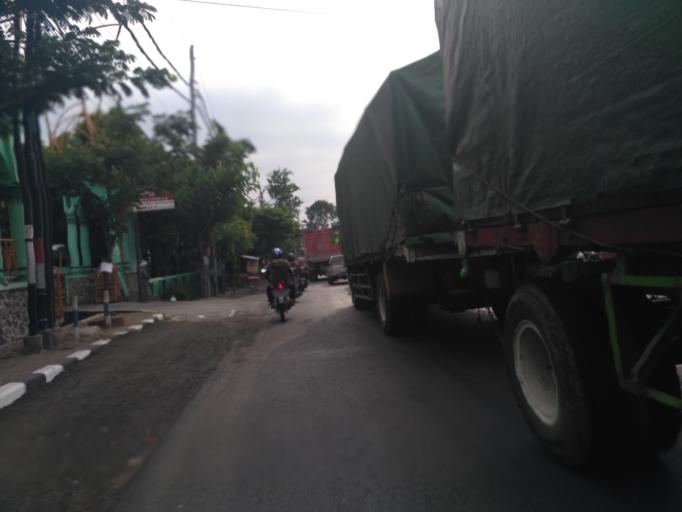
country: ID
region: Central Java
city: Semarang
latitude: -6.9865
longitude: 110.3592
